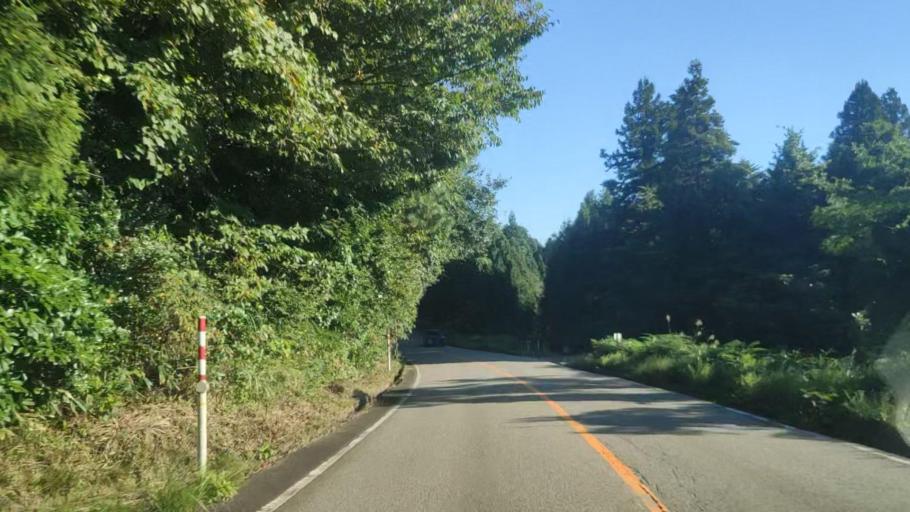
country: JP
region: Ishikawa
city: Nanao
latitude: 37.1072
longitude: 136.9463
